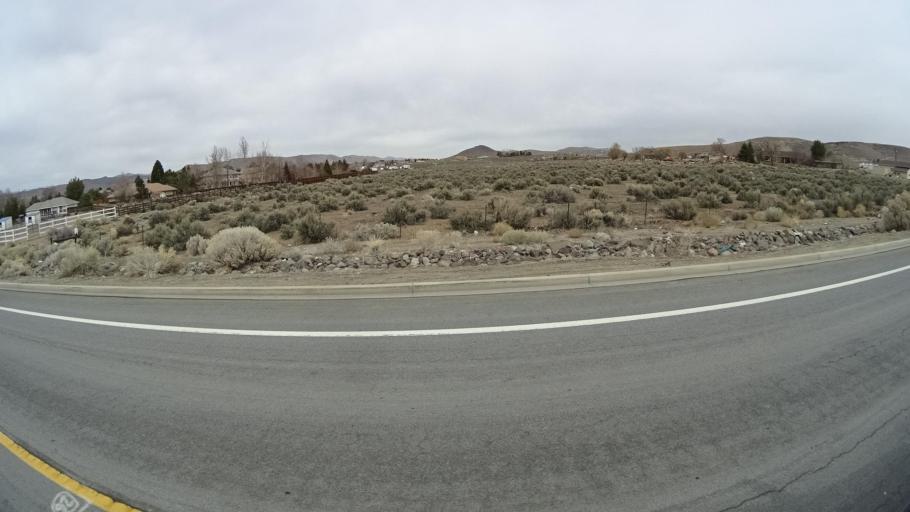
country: US
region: Nevada
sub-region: Washoe County
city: Spanish Springs
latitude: 39.6362
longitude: -119.6775
